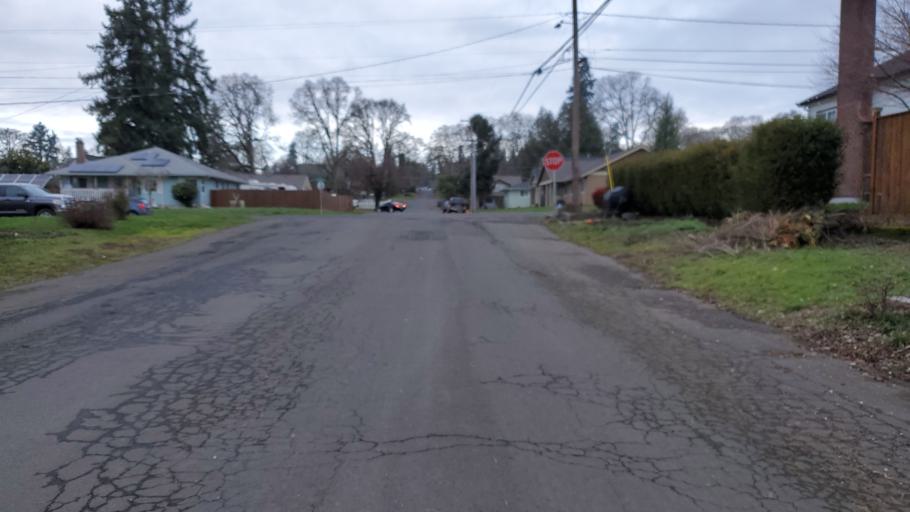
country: US
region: Oregon
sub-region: Clackamas County
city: Gladstone
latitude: 45.3826
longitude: -122.5862
